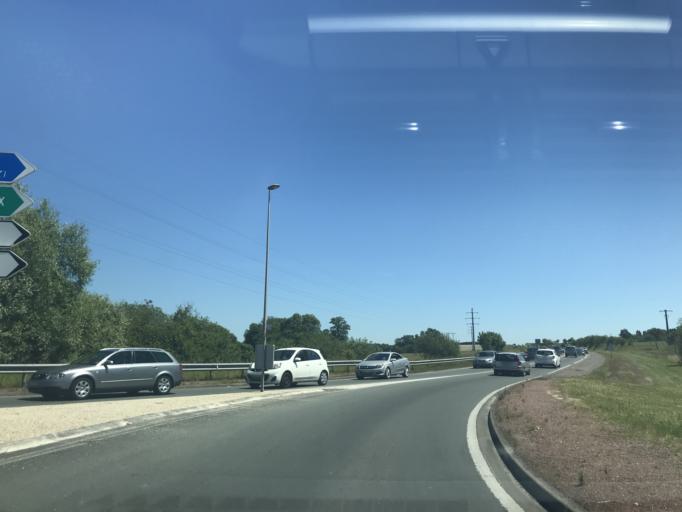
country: FR
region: Poitou-Charentes
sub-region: Departement de la Charente-Maritime
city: Saint-Georges-de-Didonne
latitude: 45.6161
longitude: -0.9880
